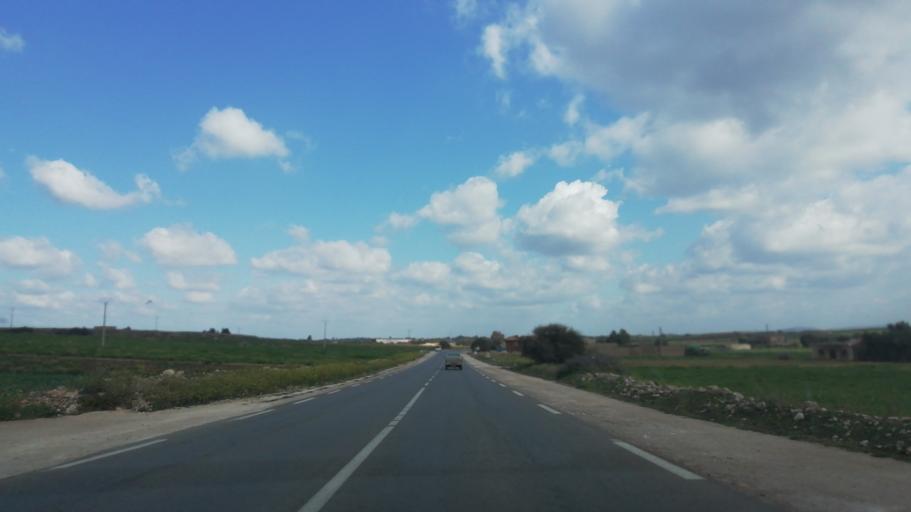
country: DZ
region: Relizane
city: Relizane
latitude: 35.7129
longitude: 0.2811
